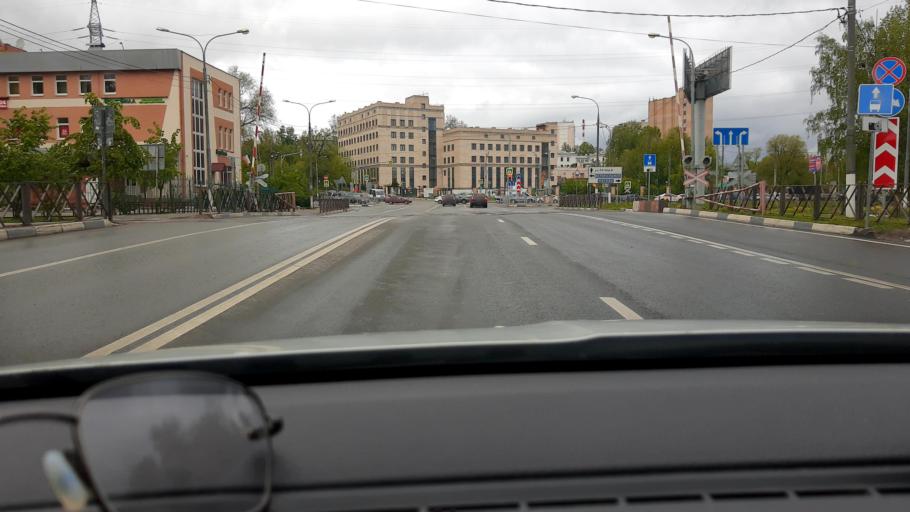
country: RU
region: Moskovskaya
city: Pavshino
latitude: 55.8175
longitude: 37.3410
